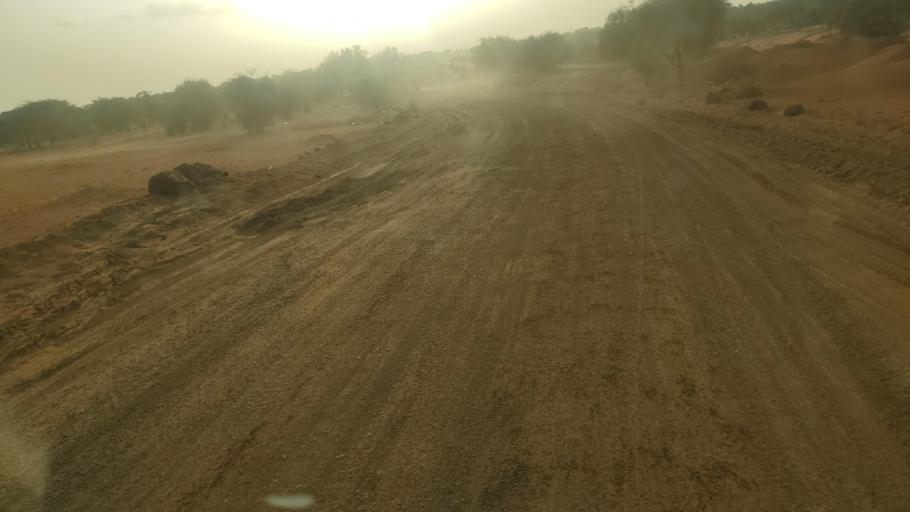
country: SN
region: Louga
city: Dara
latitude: 15.3548
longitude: -15.5321
